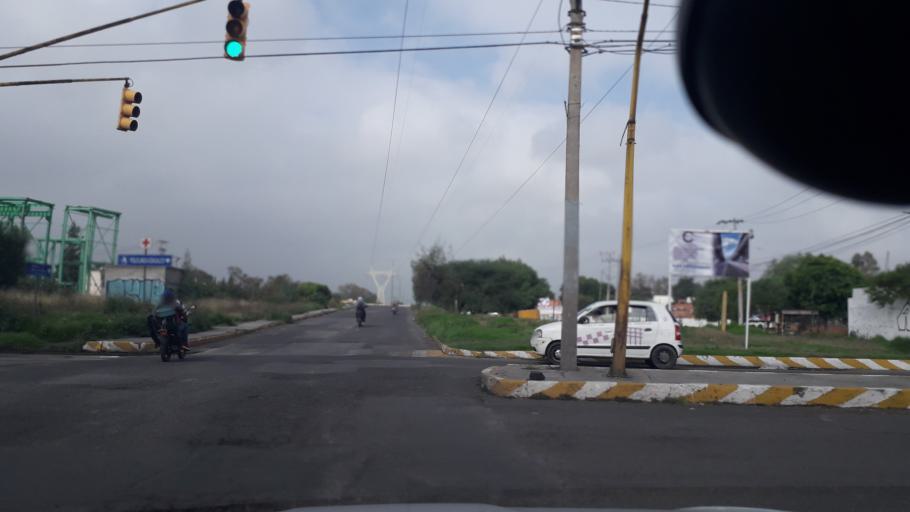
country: MX
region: Mexico
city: Coacalco
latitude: 19.6444
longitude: -99.0906
